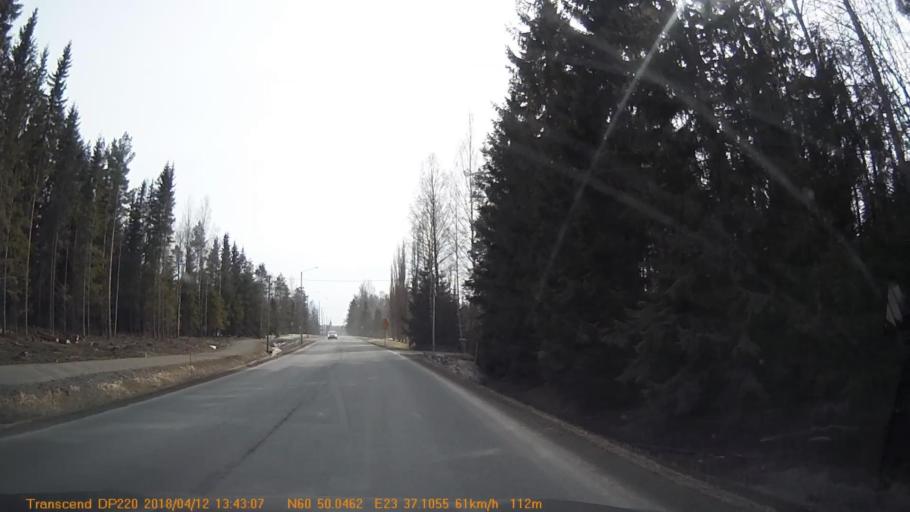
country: FI
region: Haeme
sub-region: Forssa
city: Forssa
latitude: 60.8336
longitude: 23.6186
